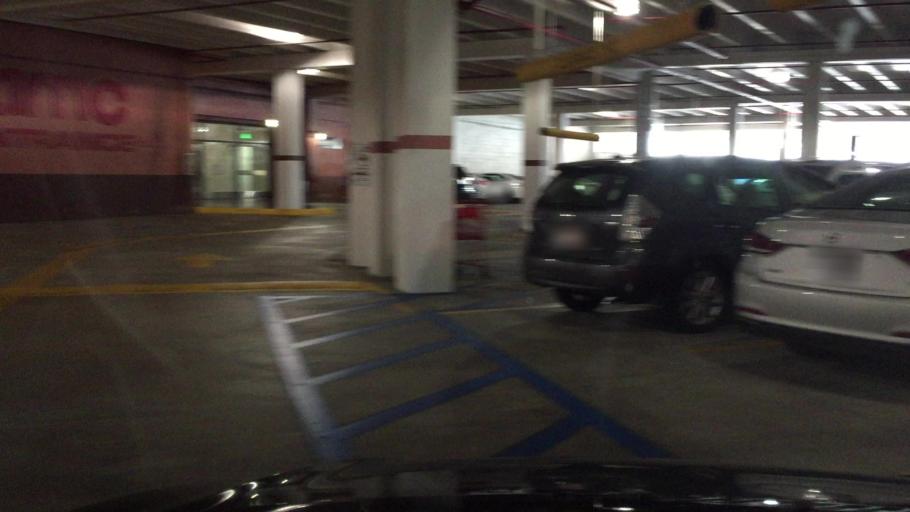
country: US
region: California
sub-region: San Diego County
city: La Jolla
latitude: 32.8660
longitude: -117.2324
